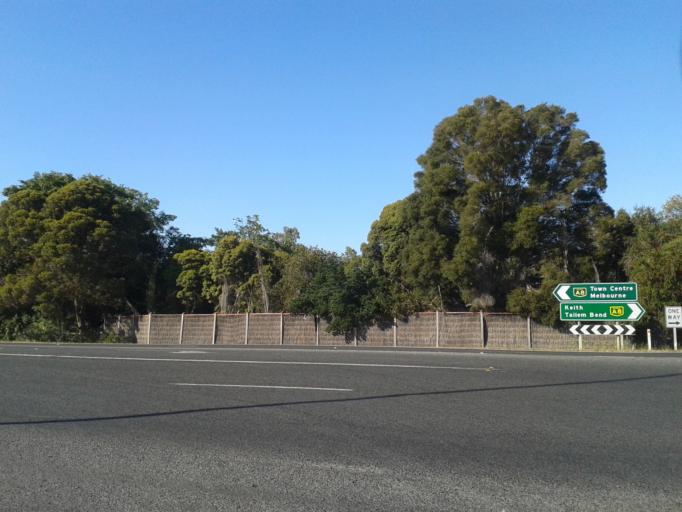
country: AU
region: South Australia
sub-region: Tatiara
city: Bordertown
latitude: -36.3028
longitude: 140.7653
